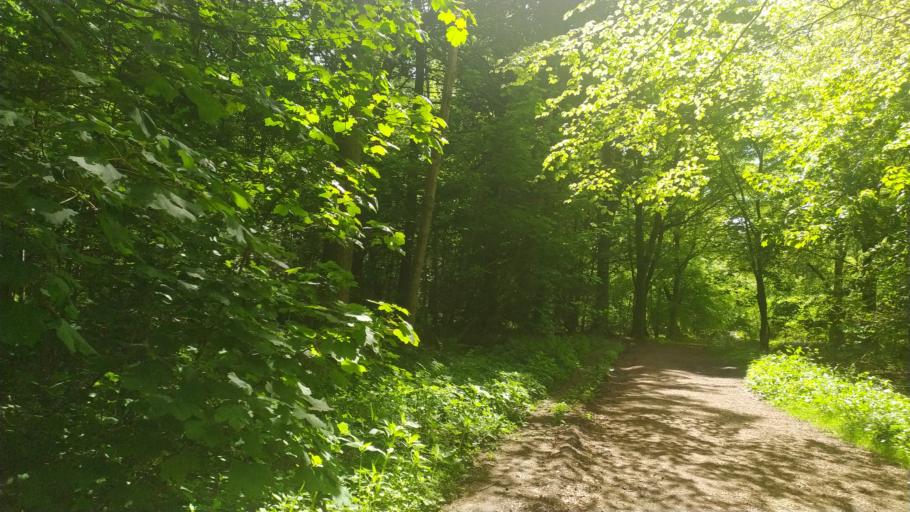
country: GB
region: England
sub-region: City and Borough of Leeds
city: Shadwell
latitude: 53.8964
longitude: -1.5115
